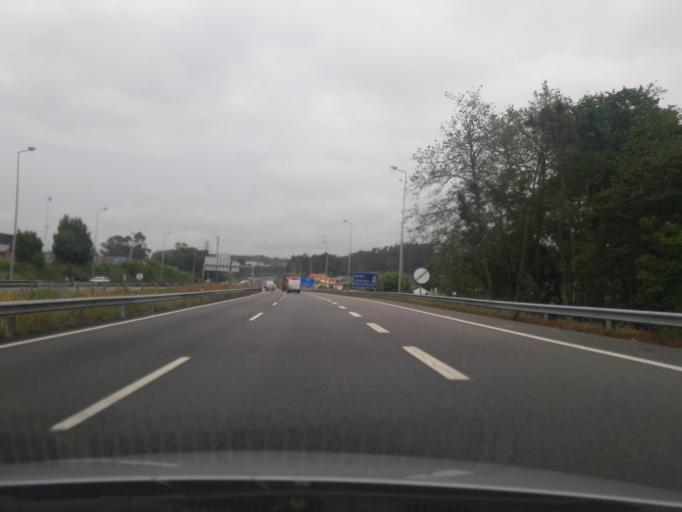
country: PT
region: Porto
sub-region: Vila do Conde
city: Arvore
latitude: 41.3289
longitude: -8.7088
